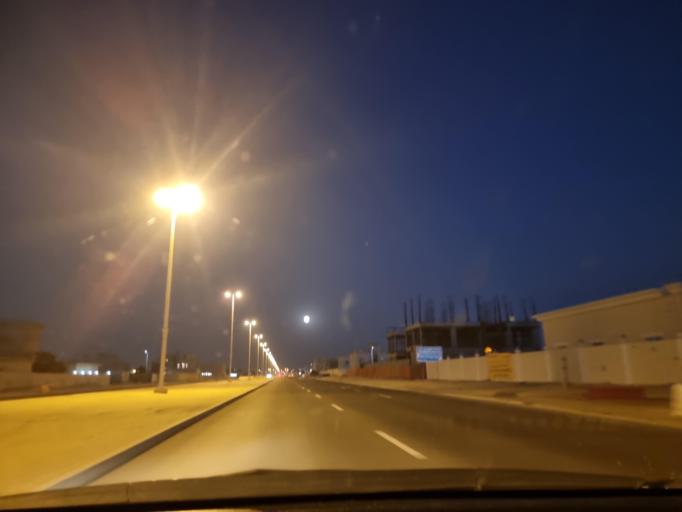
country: AE
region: Abu Dhabi
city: Abu Dhabi
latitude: 24.3162
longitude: 54.5641
